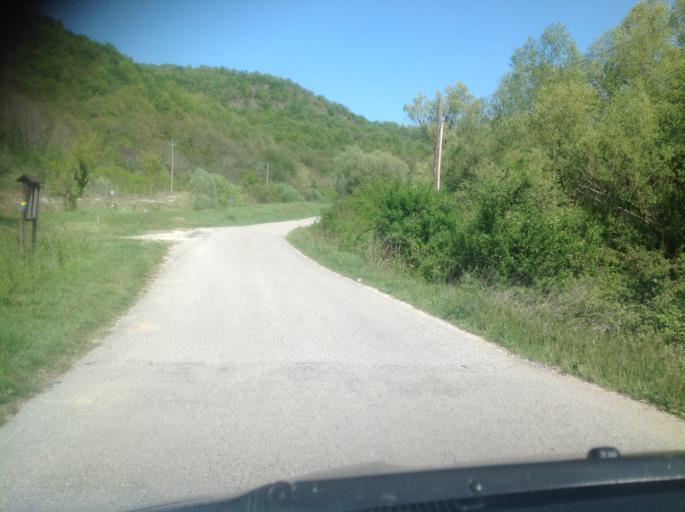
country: IT
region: Latium
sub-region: Provincia di Rieti
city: Colli sul Velino
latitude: 42.4934
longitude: 12.7835
